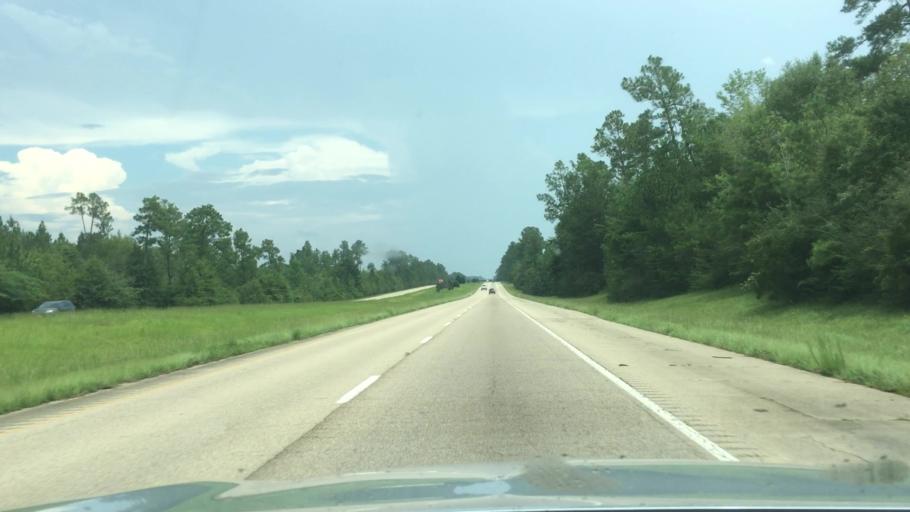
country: US
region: Mississippi
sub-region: Lamar County
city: Lumberton
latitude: 30.9692
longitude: -89.4346
